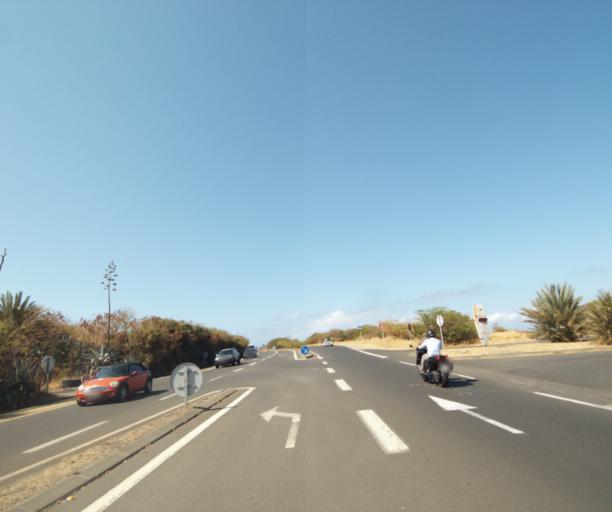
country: RE
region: Reunion
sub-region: Reunion
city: Trois-Bassins
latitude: -21.1113
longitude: 55.2560
